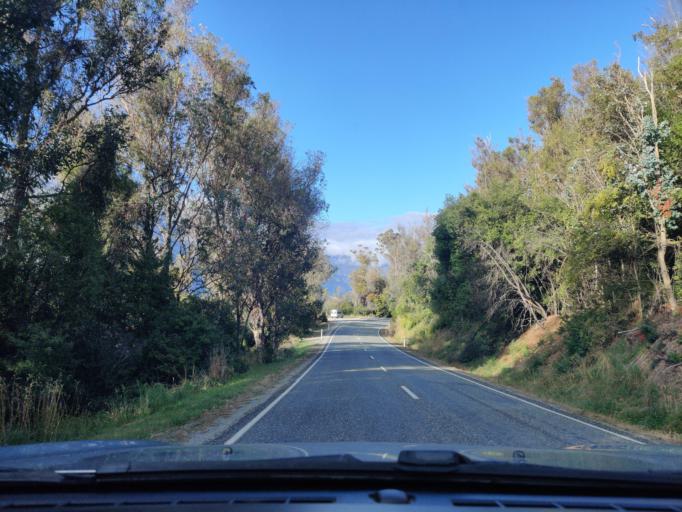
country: NZ
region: Otago
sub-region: Queenstown-Lakes District
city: Queenstown
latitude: -45.0434
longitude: 168.6340
